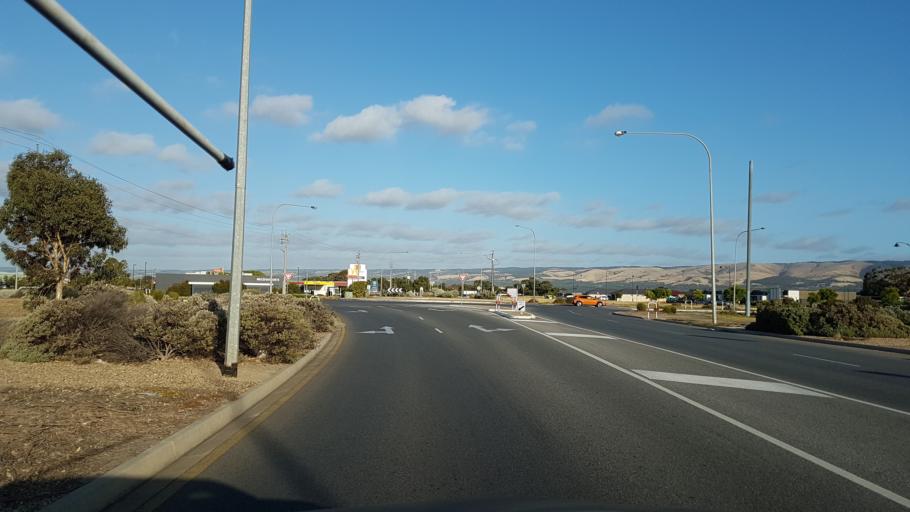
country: AU
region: South Australia
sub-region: Onkaparinga
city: Port Willunga
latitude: -35.2787
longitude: 138.4572
